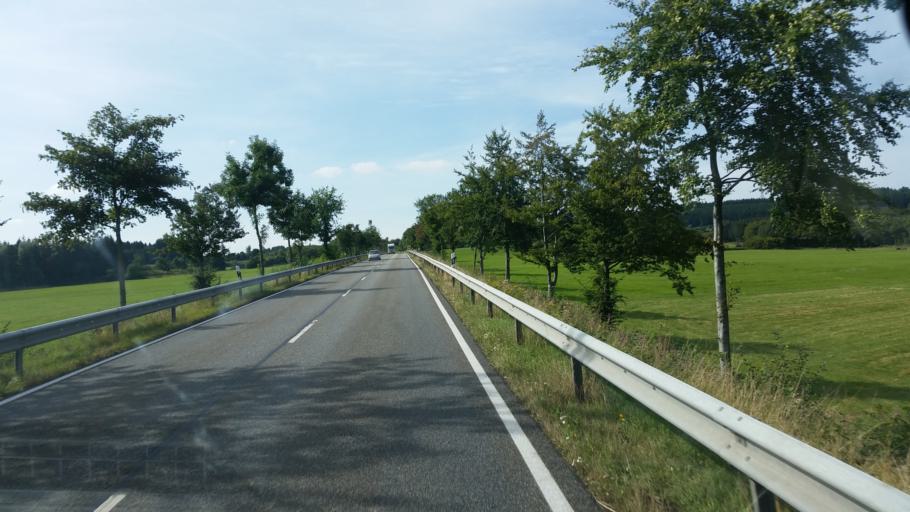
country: DE
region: Rheinland-Pfalz
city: Bretthausen
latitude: 50.6602
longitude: 8.0675
